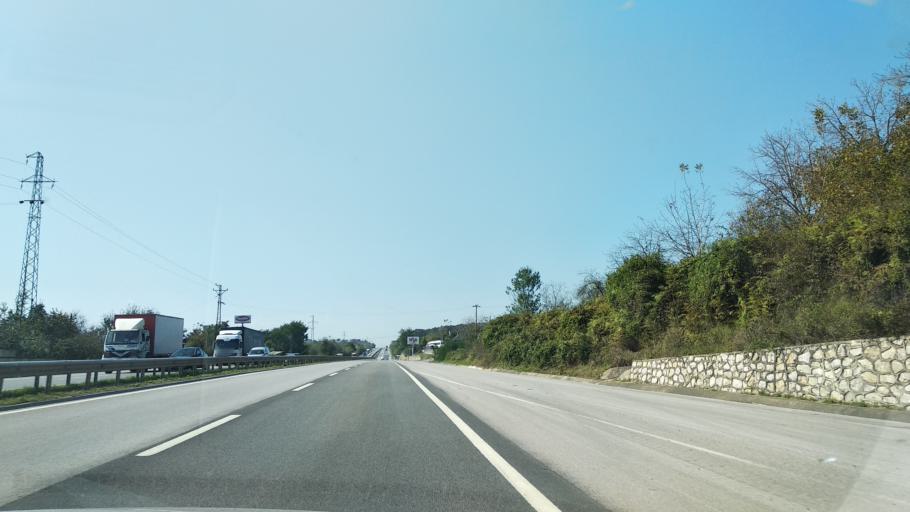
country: TR
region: Kocaeli
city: Derbent
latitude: 40.7319
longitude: 30.1775
